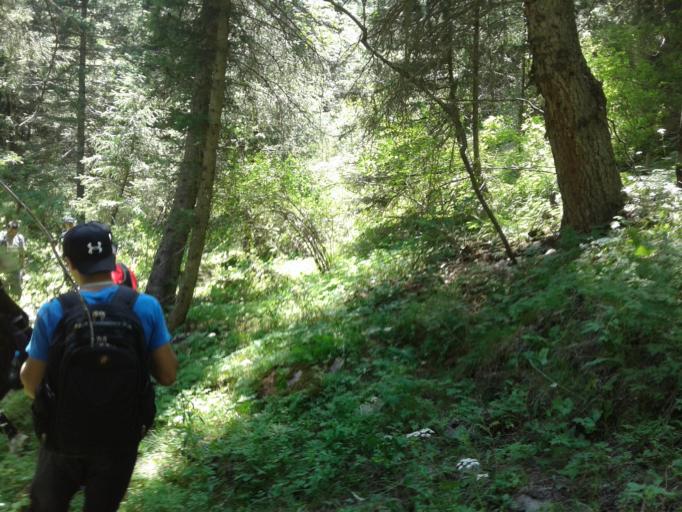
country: KG
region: Naryn
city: Naryn
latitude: 41.4184
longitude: 76.1855
